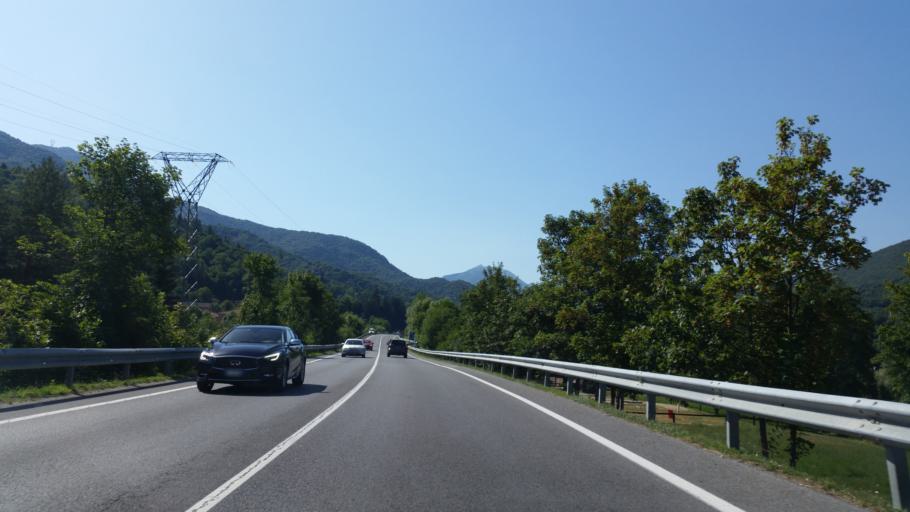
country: IT
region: Piedmont
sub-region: Provincia di Cuneo
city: Robilante
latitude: 44.2947
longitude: 7.5165
